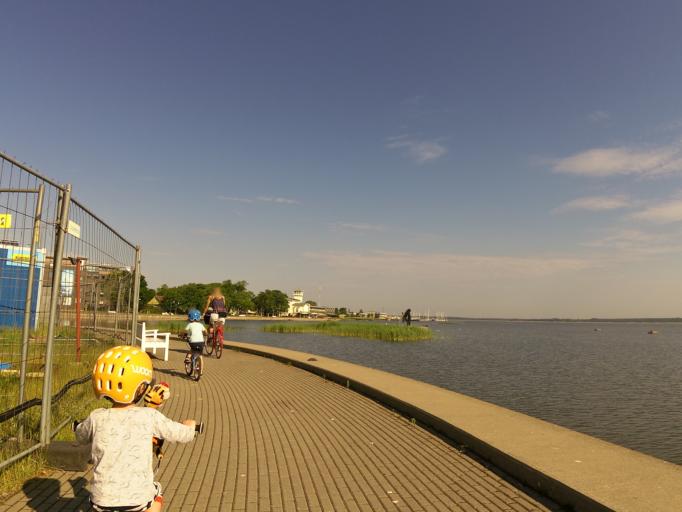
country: EE
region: Laeaene
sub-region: Haapsalu linn
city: Haapsalu
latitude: 58.9519
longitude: 23.5357
